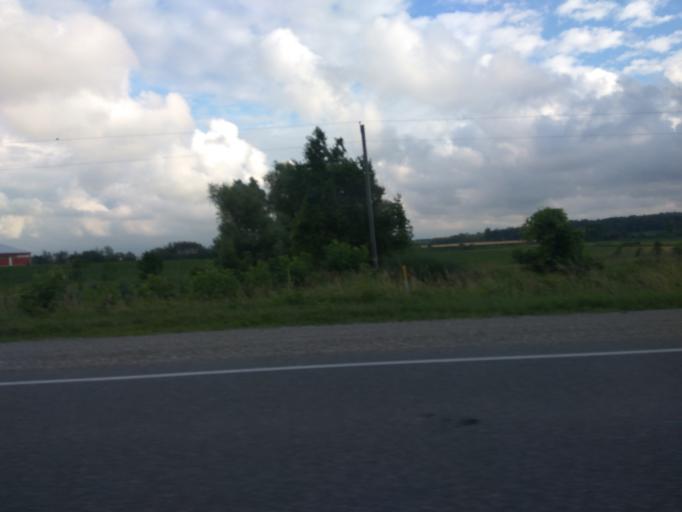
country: CA
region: Ontario
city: Stratford
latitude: 43.3691
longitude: -80.7917
